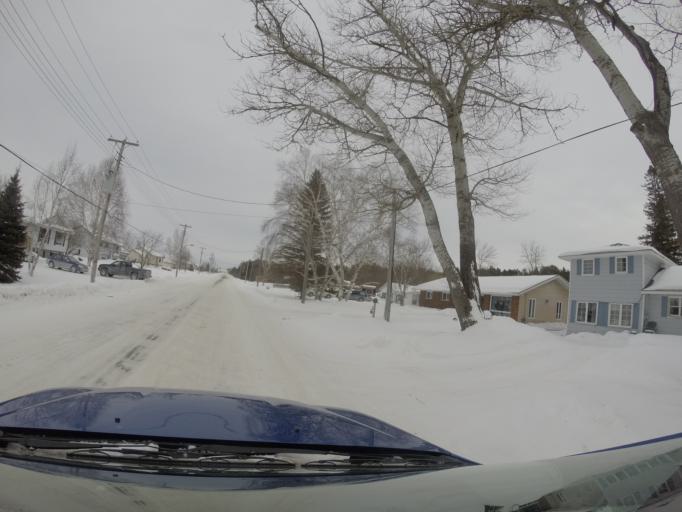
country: CA
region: Ontario
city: Wasaga Beach
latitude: 44.4211
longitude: -80.0696
